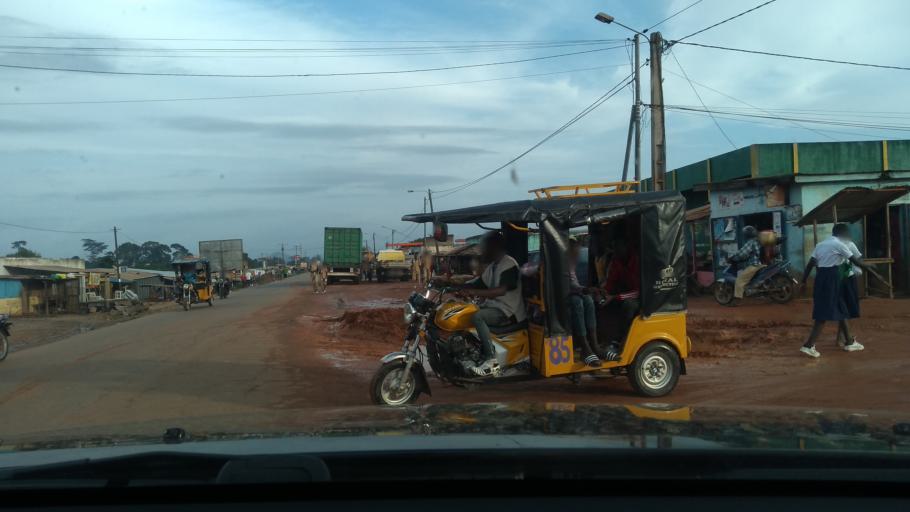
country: CI
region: Bas-Sassandra
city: Soubre
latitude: 5.3995
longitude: -6.5517
